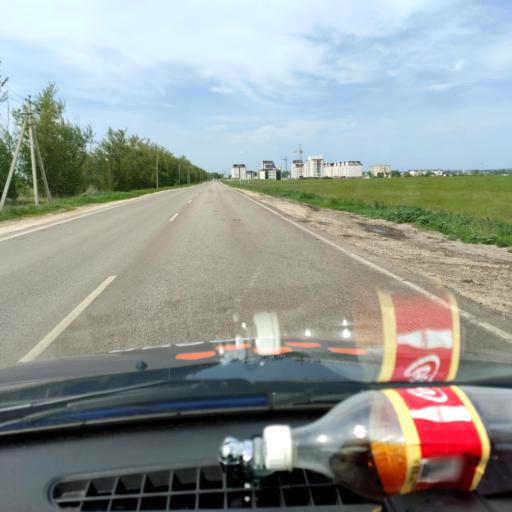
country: RU
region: Voronezj
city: Novaya Usman'
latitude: 51.5952
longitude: 39.3738
